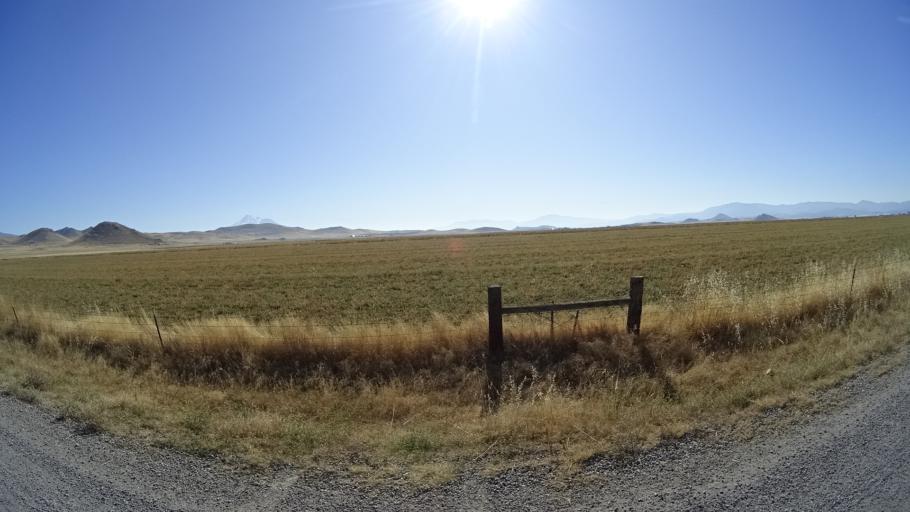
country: US
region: California
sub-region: Siskiyou County
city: Montague
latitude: 41.7865
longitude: -122.4464
